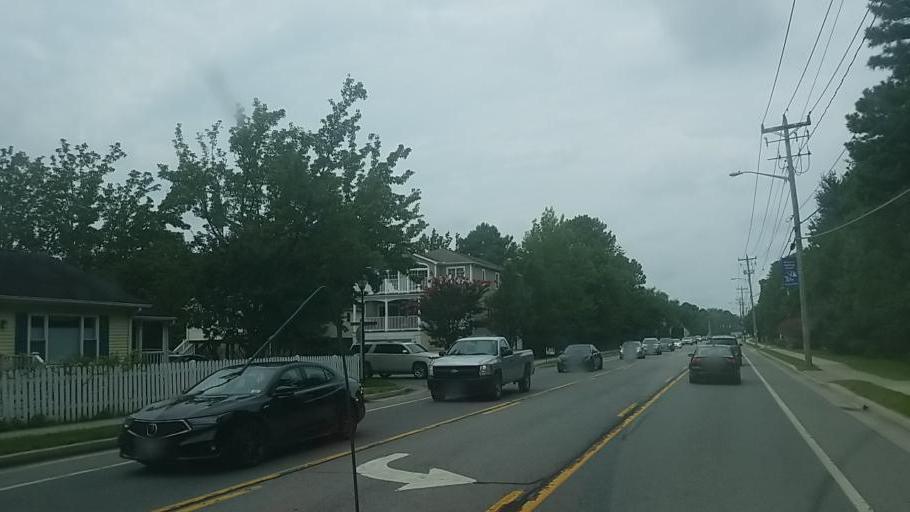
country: US
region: Delaware
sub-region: Sussex County
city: Bethany Beach
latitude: 38.5388
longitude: -75.0635
